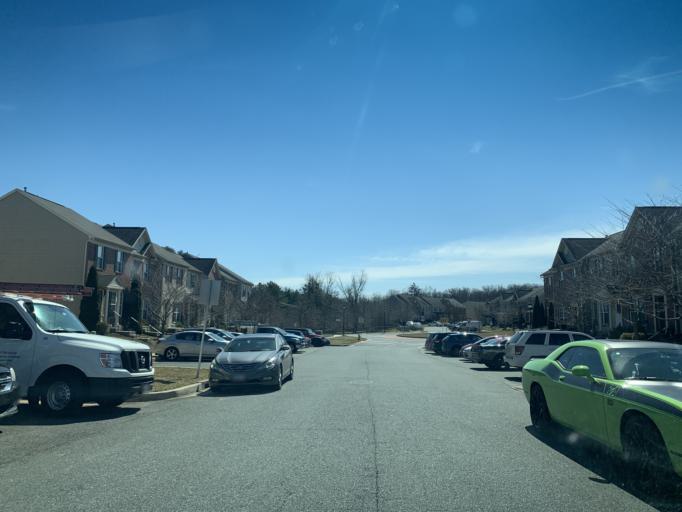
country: US
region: Maryland
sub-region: Harford County
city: Edgewood
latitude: 39.4547
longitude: -76.2897
